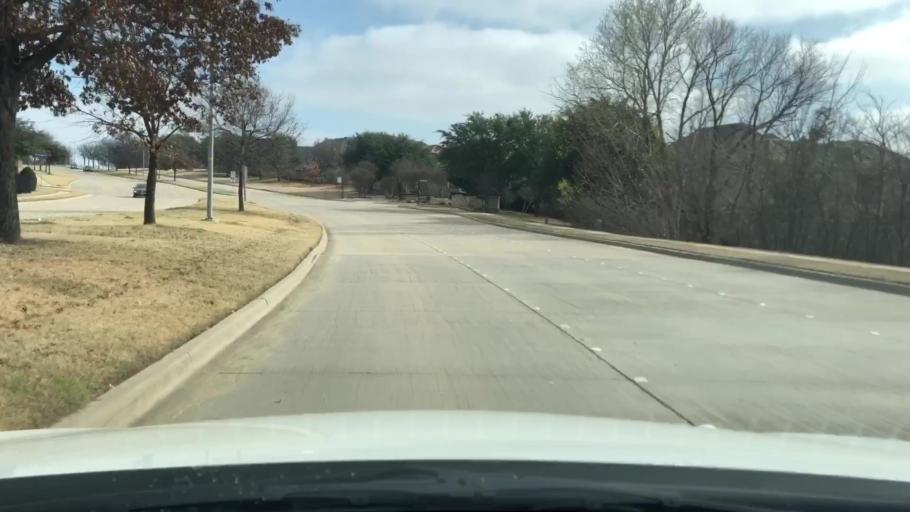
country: US
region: Texas
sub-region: Denton County
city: The Colony
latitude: 33.0695
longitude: -96.8488
